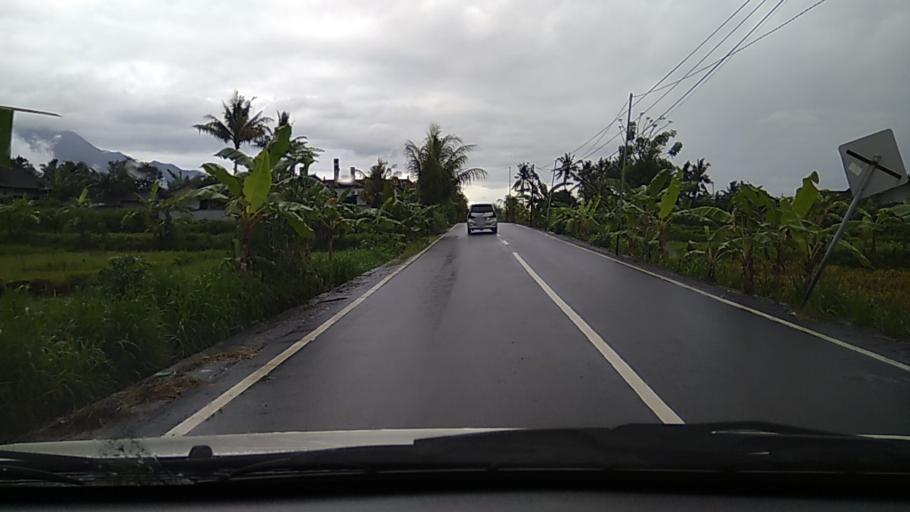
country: ID
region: Bali
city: Banjar Danginsema
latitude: -8.4639
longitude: 115.6227
